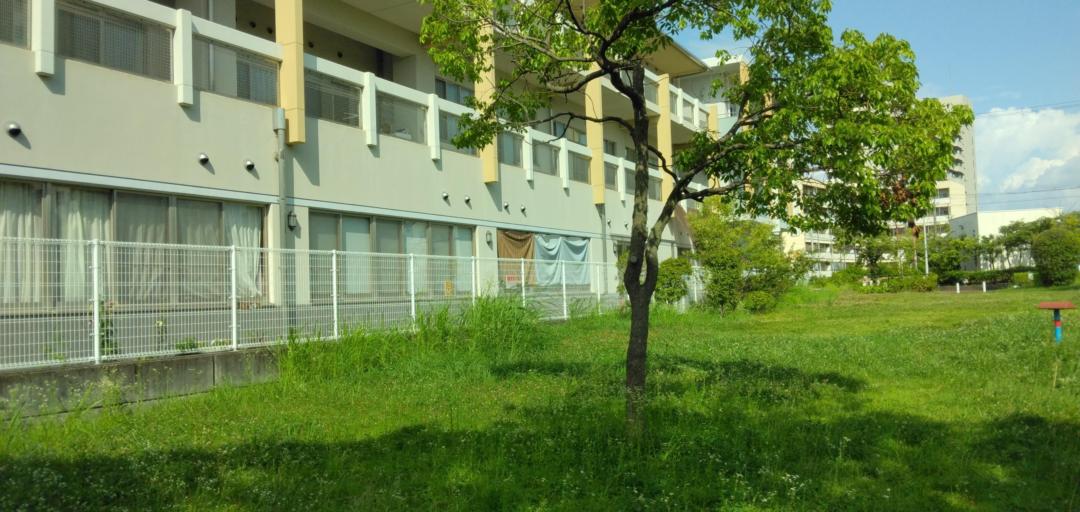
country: JP
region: Osaka
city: Sakai
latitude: 34.5638
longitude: 135.4703
